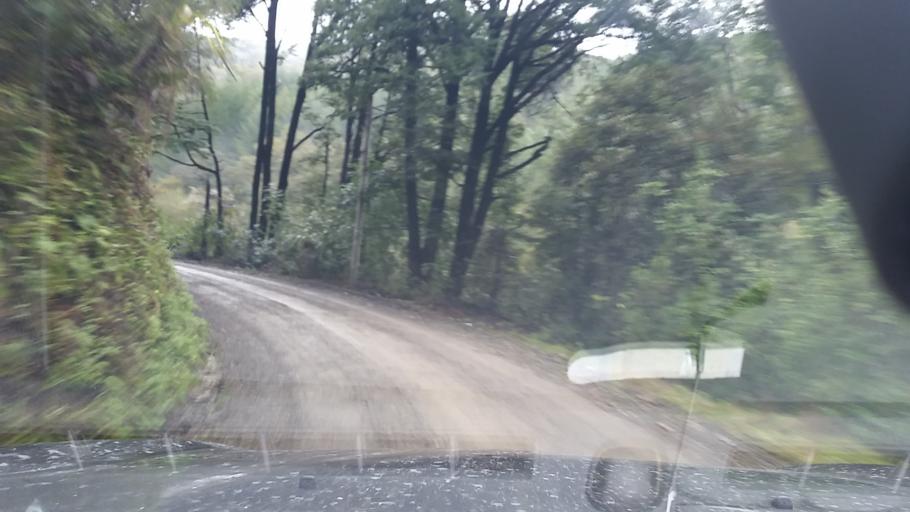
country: NZ
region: Nelson
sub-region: Nelson City
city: Nelson
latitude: -41.3700
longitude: 173.6069
